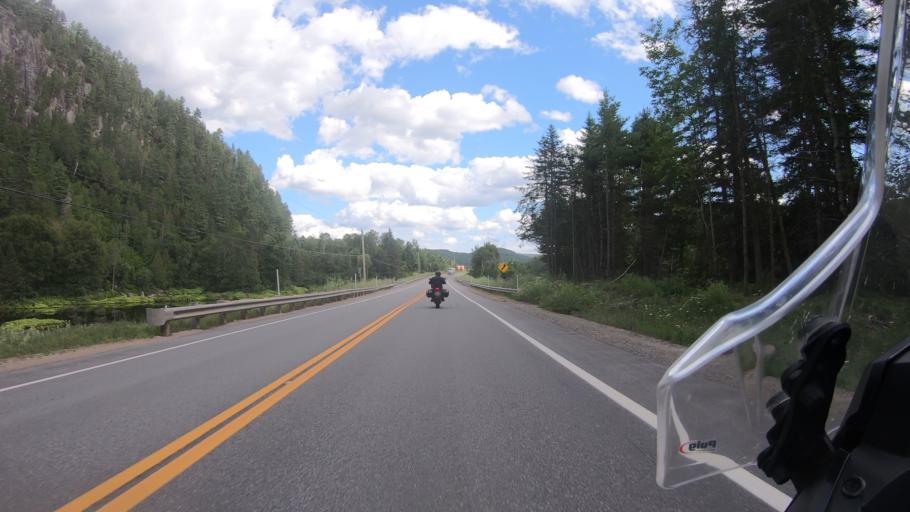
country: CA
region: Quebec
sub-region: Mauricie
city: Saint-Tite
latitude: 46.9896
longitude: -72.9128
